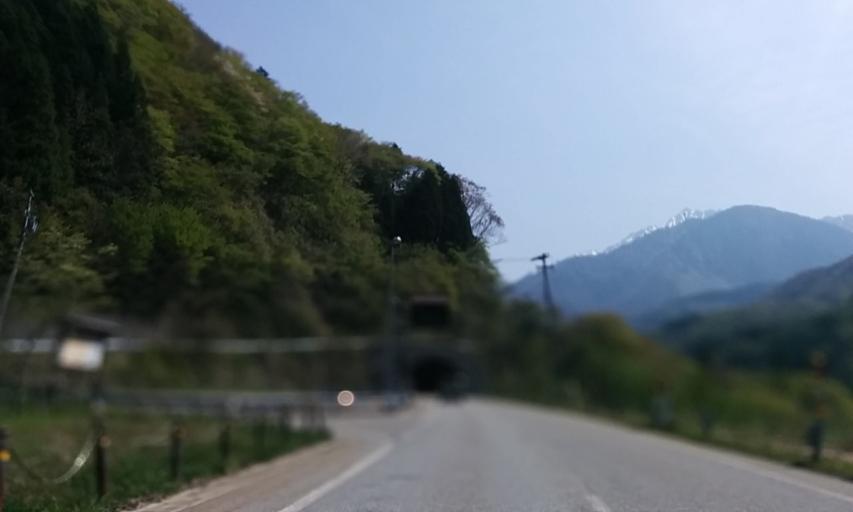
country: JP
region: Gifu
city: Takayama
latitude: 36.2548
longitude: 137.5492
